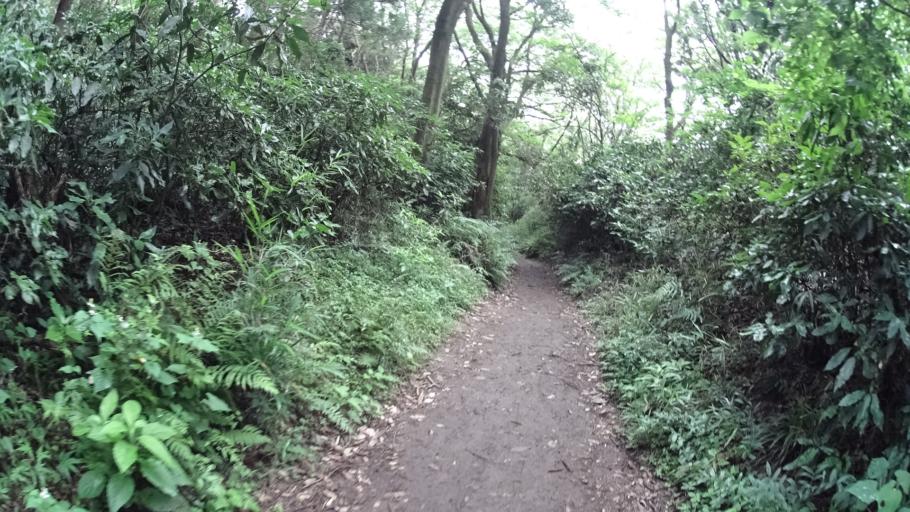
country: JP
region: Kanagawa
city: Zushi
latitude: 35.3388
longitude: 139.5881
